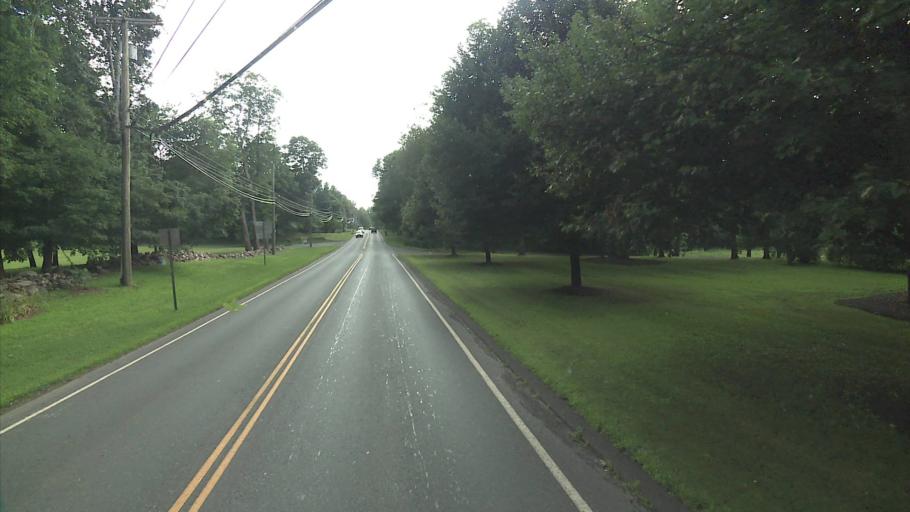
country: US
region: Connecticut
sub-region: New Haven County
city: Southbury
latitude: 41.4970
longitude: -73.2133
